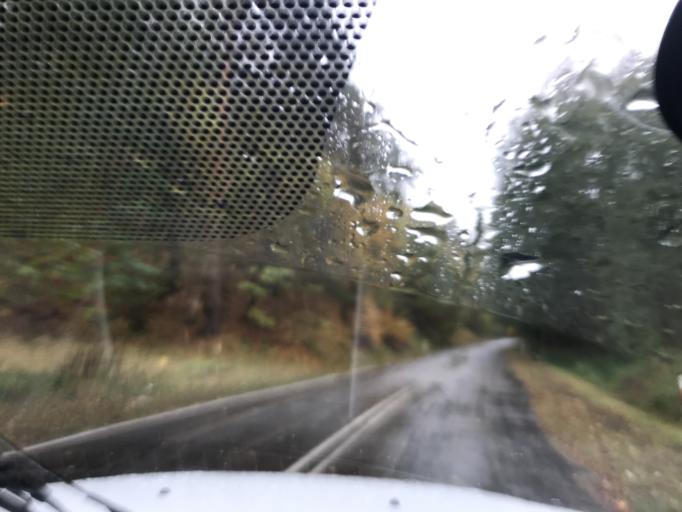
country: DE
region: Brandenburg
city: Neulewin
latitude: 52.7852
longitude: 14.2955
